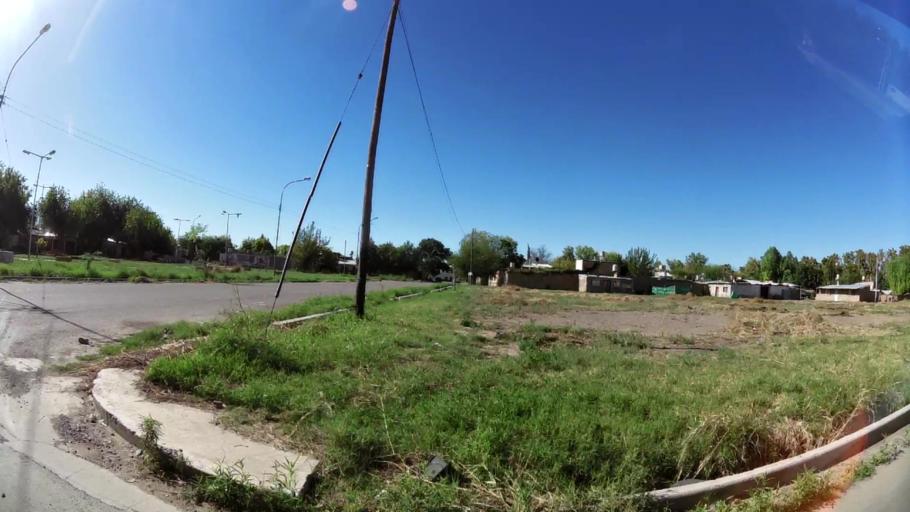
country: AR
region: Mendoza
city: Las Heras
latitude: -32.8389
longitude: -68.8271
